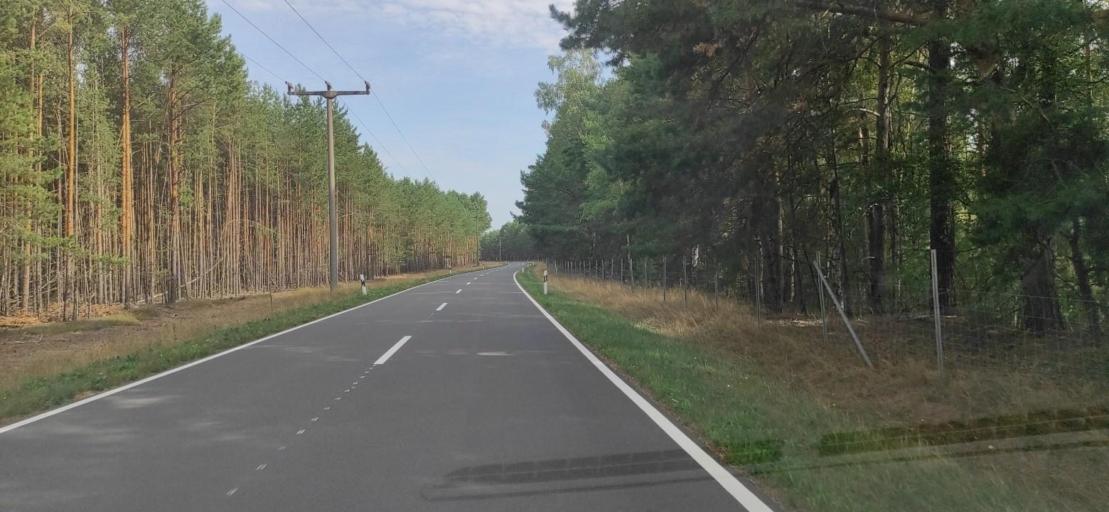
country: PL
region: Lubusz
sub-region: Powiat zarski
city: Trzebiel
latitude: 51.6456
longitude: 14.7459
